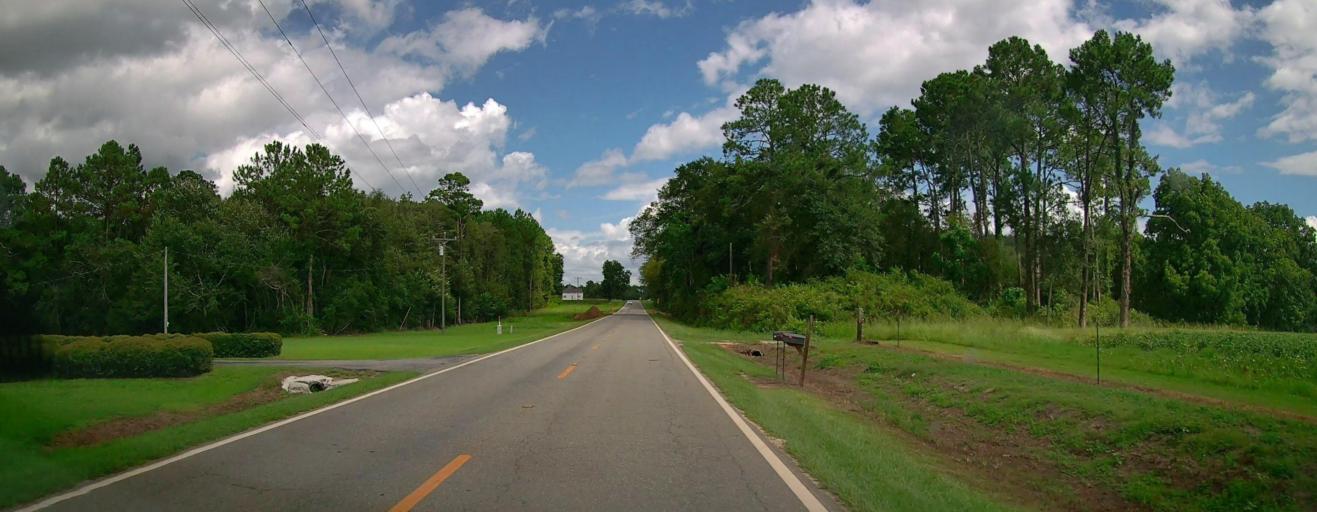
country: US
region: Georgia
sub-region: Ben Hill County
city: Fitzgerald
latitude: 31.6818
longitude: -83.2027
